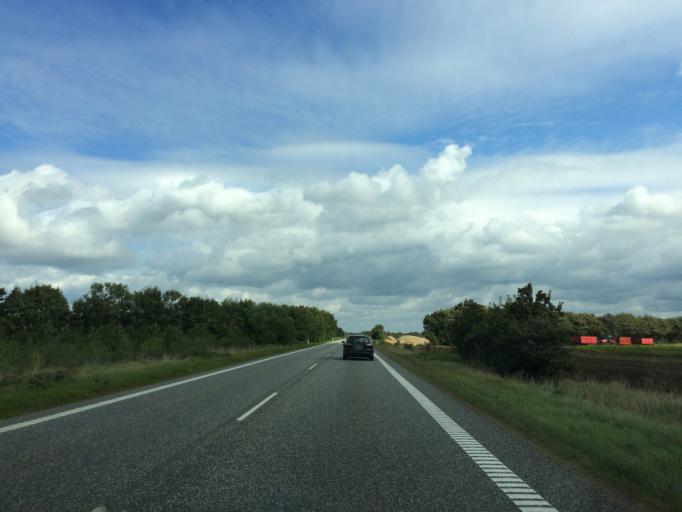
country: DK
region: Central Jutland
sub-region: Holstebro Kommune
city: Vinderup
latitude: 56.3778
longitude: 8.7599
